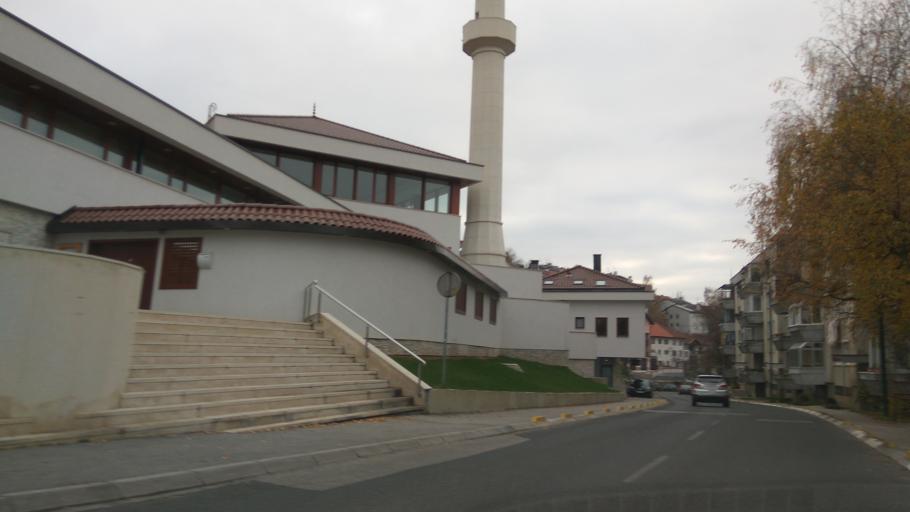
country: BA
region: Federation of Bosnia and Herzegovina
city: Kobilja Glava
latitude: 43.8666
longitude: 18.4053
